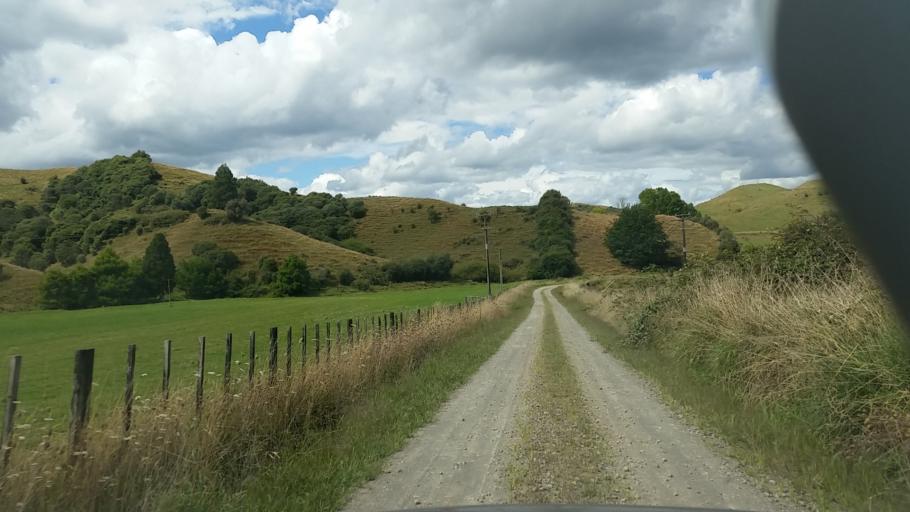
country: NZ
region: Taranaki
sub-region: South Taranaki District
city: Eltham
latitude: -39.2572
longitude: 174.5639
